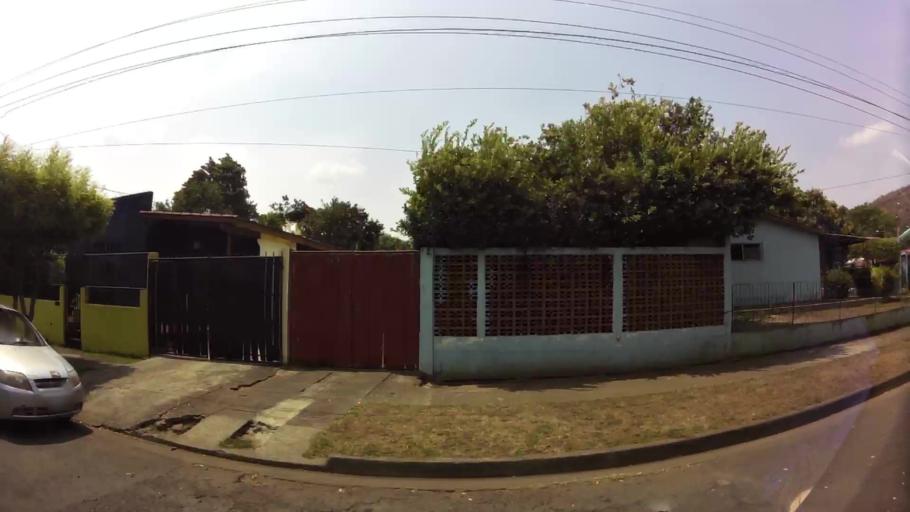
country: NI
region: Managua
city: Ciudad Sandino
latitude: 12.1565
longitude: -86.3143
